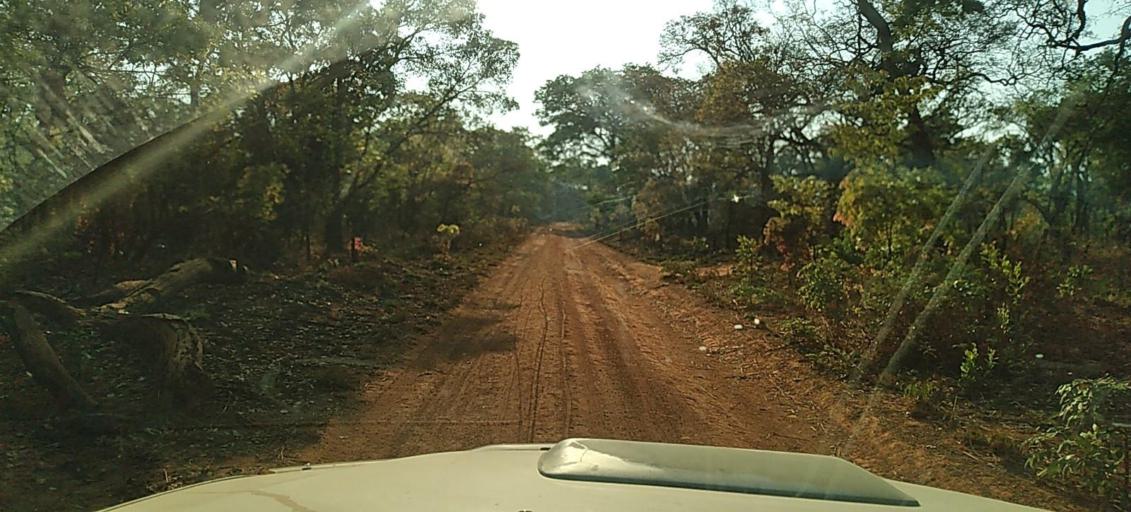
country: ZM
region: North-Western
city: Kasempa
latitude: -13.1673
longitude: 25.8859
